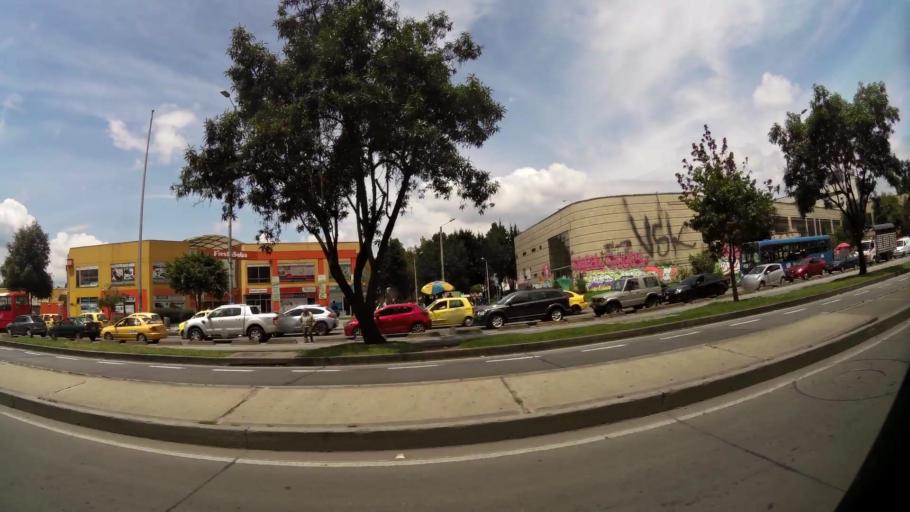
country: CO
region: Cundinamarca
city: Cota
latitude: 4.7435
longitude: -74.0924
